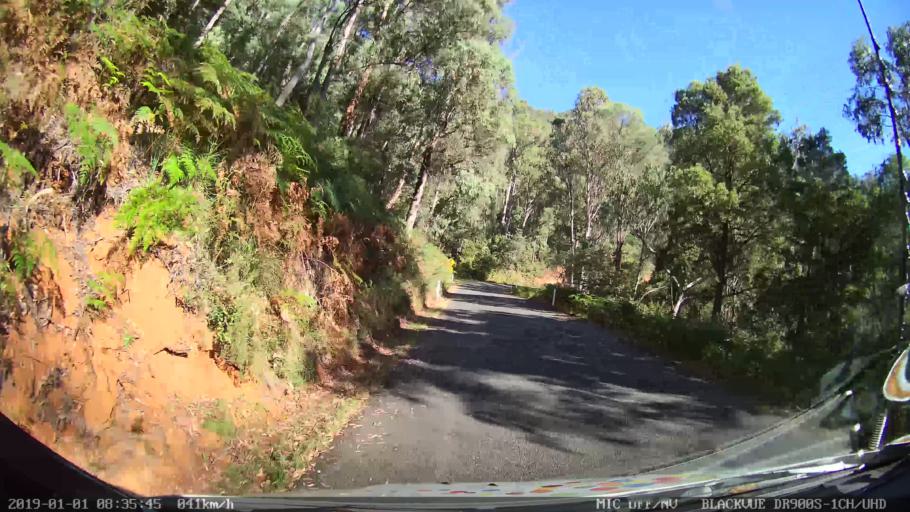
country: AU
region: New South Wales
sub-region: Snowy River
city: Jindabyne
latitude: -36.3475
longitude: 148.1937
